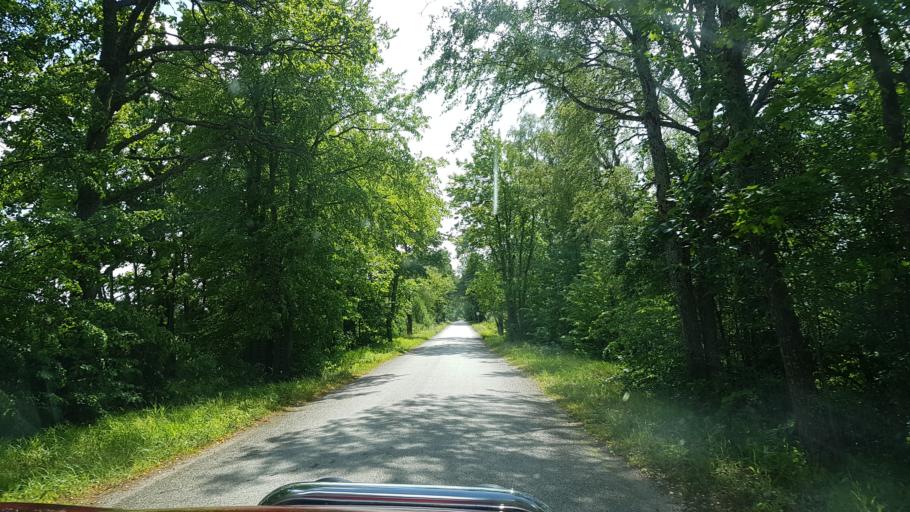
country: EE
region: Laeaene
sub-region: Lihula vald
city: Lihula
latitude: 58.5872
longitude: 23.5374
